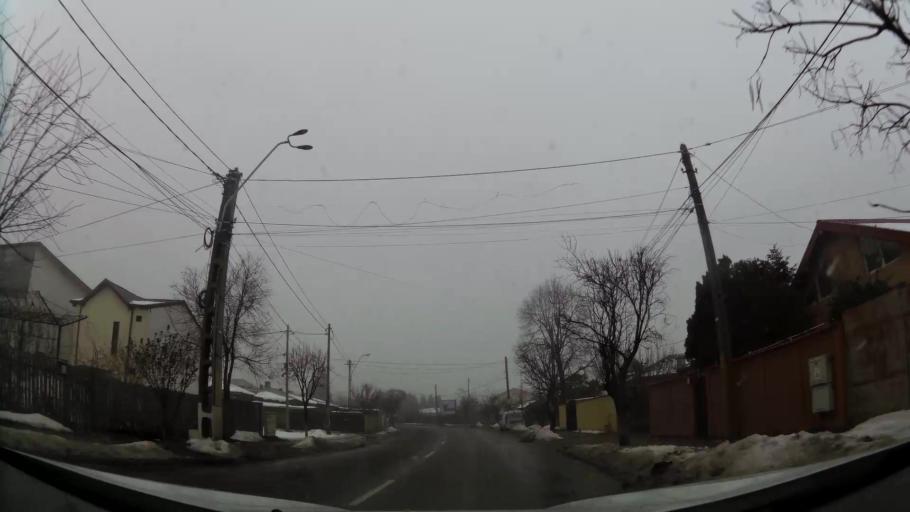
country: RO
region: Ilfov
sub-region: Comuna Chiajna
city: Chiajna
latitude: 44.4557
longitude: 25.9873
